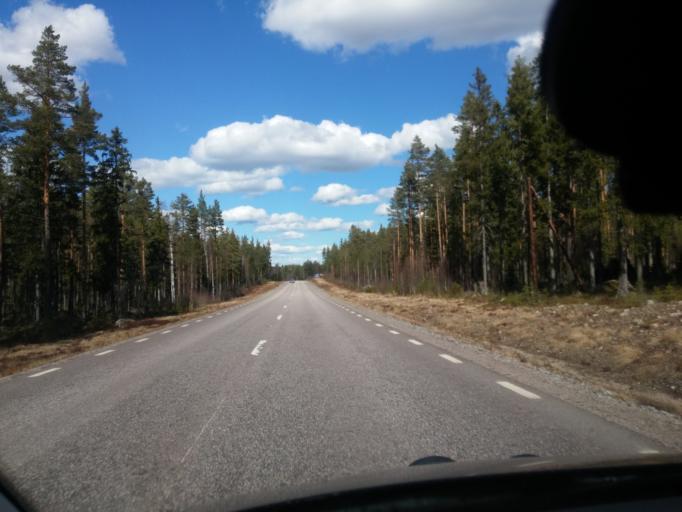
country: SE
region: Gaevleborg
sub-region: Ovanakers Kommun
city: Edsbyn
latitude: 61.2650
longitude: 15.8892
